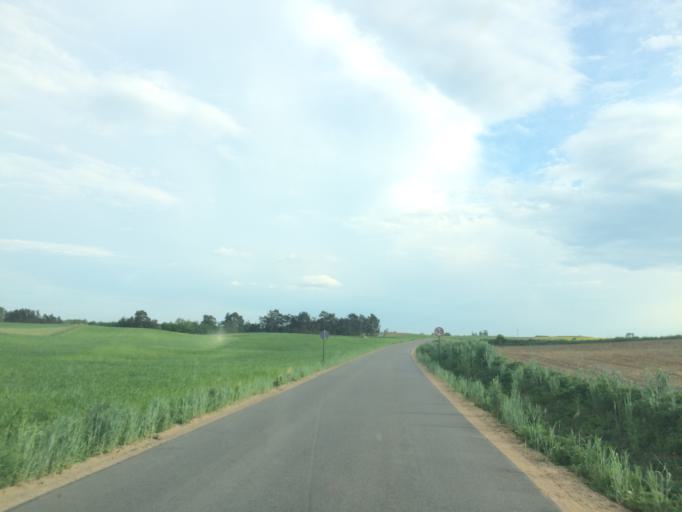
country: PL
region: Kujawsko-Pomorskie
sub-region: Powiat brodnicki
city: Brzozie
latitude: 53.3740
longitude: 19.7105
